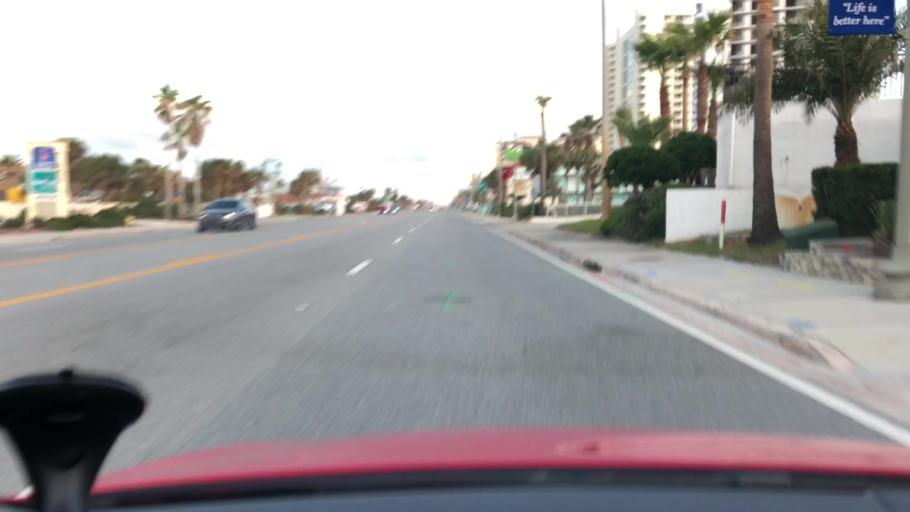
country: US
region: Florida
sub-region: Volusia County
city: Daytona Beach Shores
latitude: 29.1826
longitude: -80.9862
